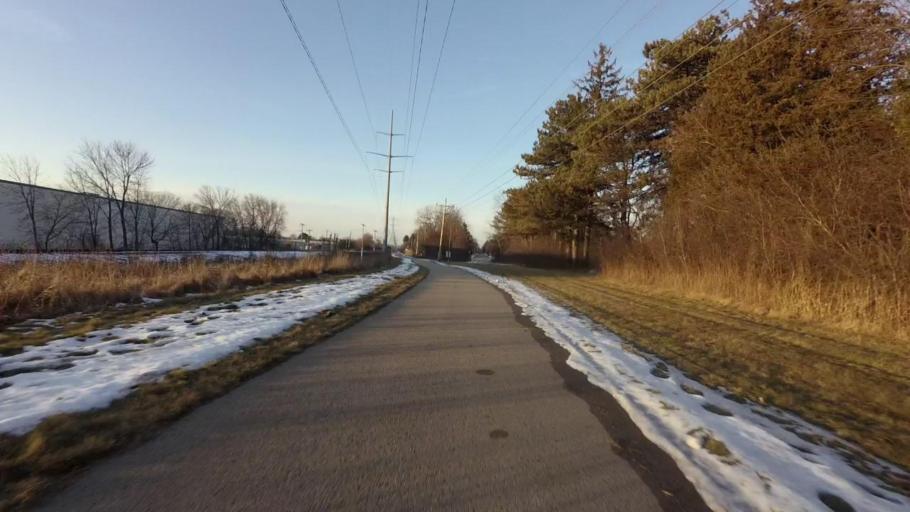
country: US
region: Wisconsin
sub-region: Milwaukee County
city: Brown Deer
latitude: 43.1620
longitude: -87.9603
